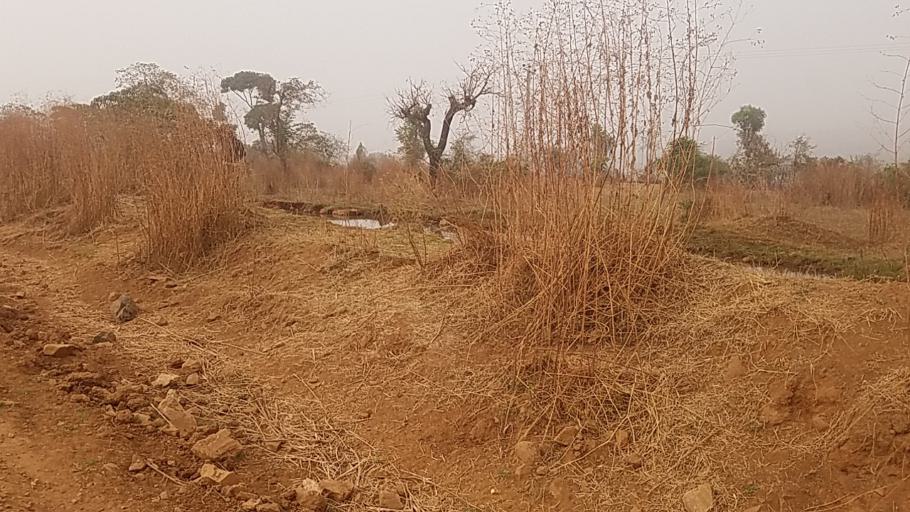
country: ET
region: Amhara
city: Bure
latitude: 10.9229
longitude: 36.4663
